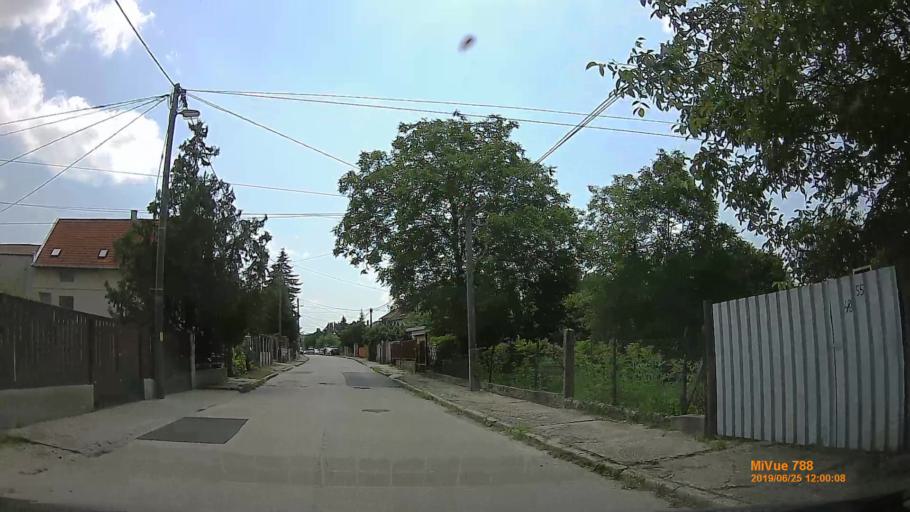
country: HU
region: Komarom-Esztergom
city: Dorog
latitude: 47.7288
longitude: 18.7346
